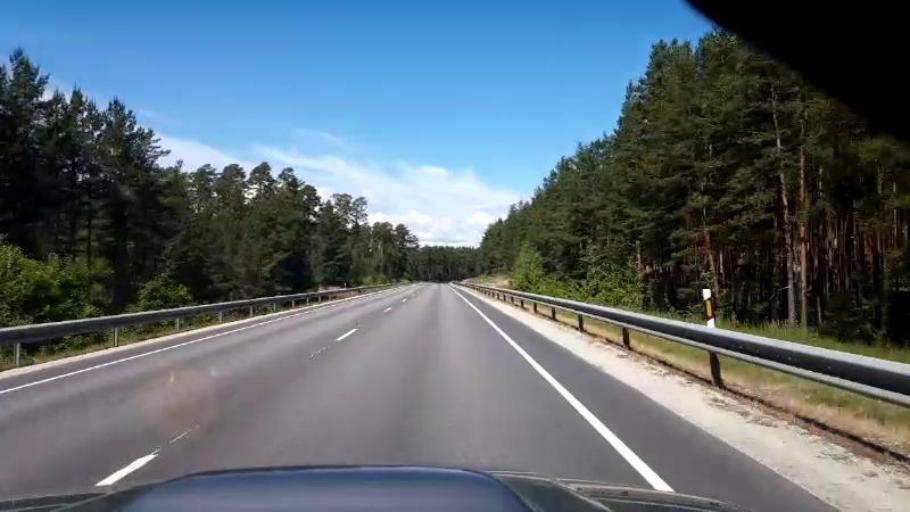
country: EE
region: Paernumaa
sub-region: Paernu linn
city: Parnu
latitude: 58.1392
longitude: 24.5074
